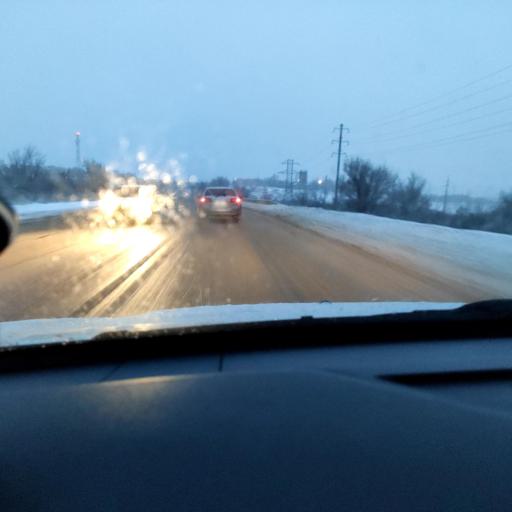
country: RU
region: Samara
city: Smyshlyayevka
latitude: 53.2443
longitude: 50.4769
